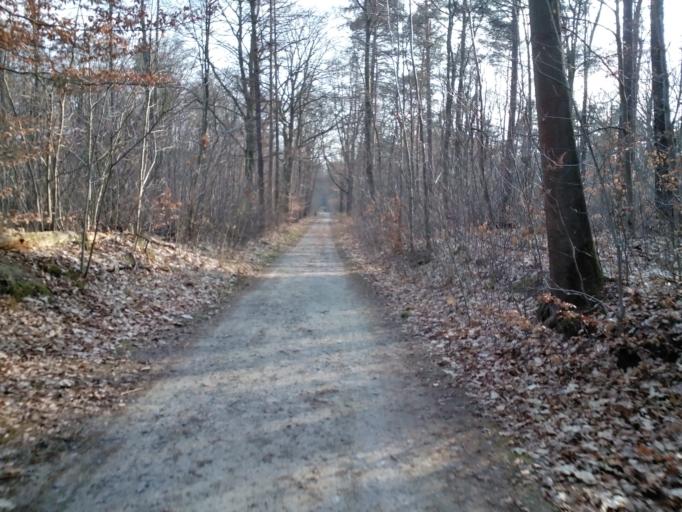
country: BE
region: Flanders
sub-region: Provincie Vlaams-Brabant
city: Oud-Heverlee
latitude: 50.8357
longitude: 4.6902
